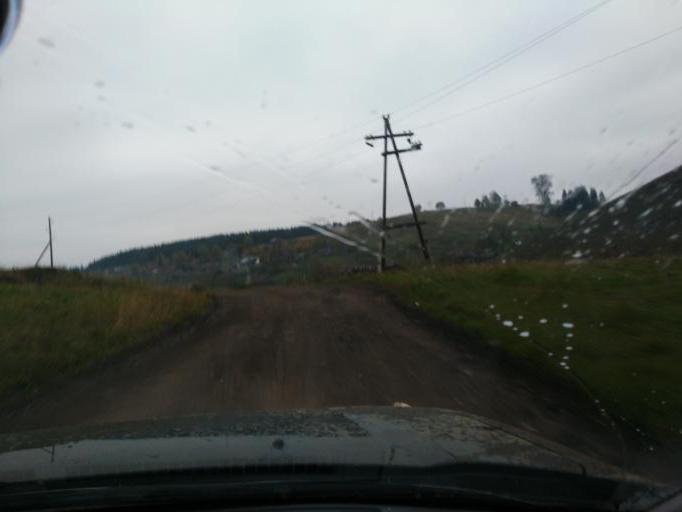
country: RU
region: Sverdlovsk
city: Sylva
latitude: 57.8664
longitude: 58.6413
